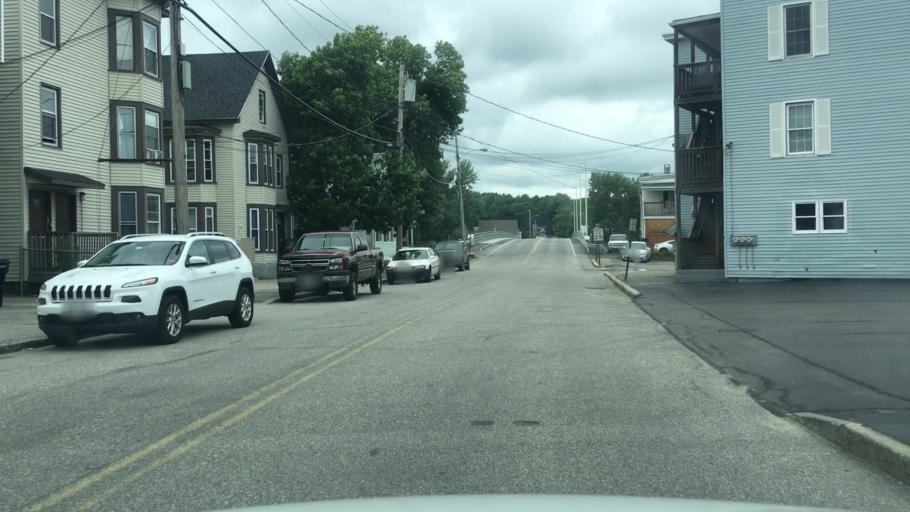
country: US
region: Maine
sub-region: York County
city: Biddeford
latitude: 43.4982
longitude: -70.4553
